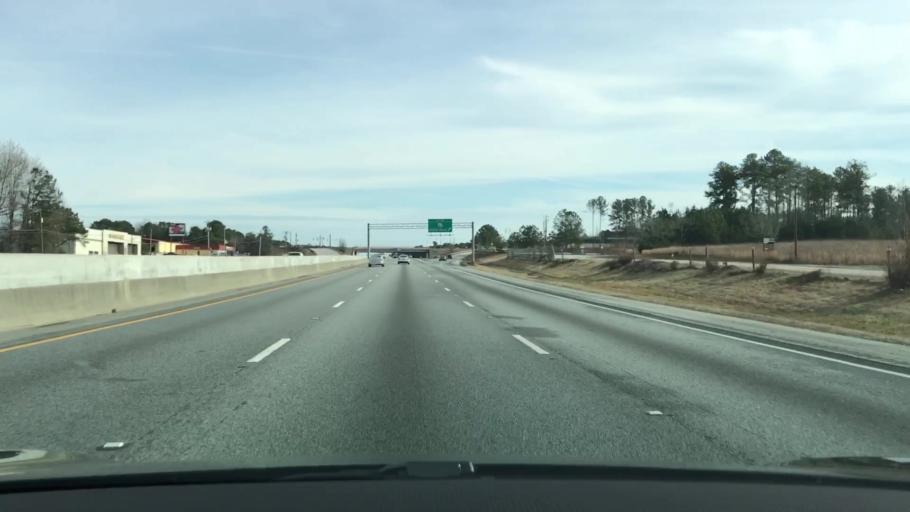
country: US
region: Georgia
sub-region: Rockdale County
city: Conyers
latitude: 33.6390
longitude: -83.9831
